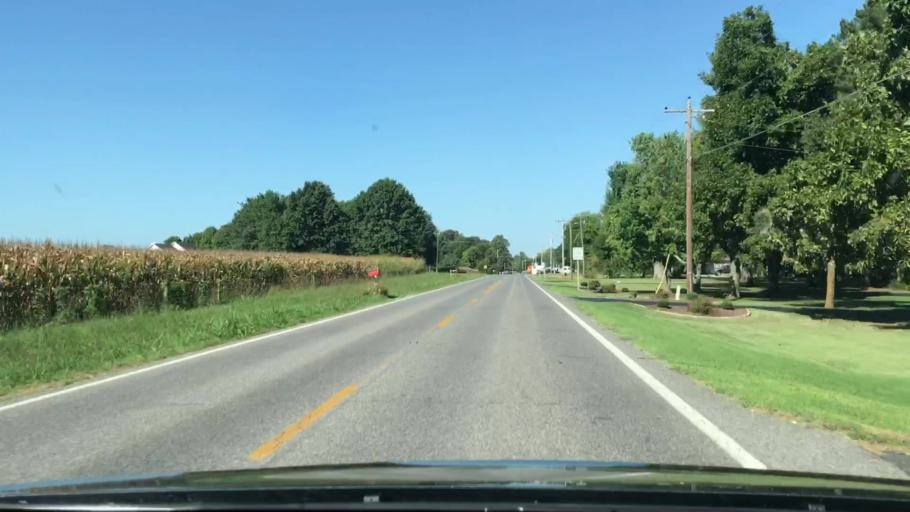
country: US
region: Kentucky
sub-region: Graves County
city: Mayfield
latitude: 36.7603
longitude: -88.5910
